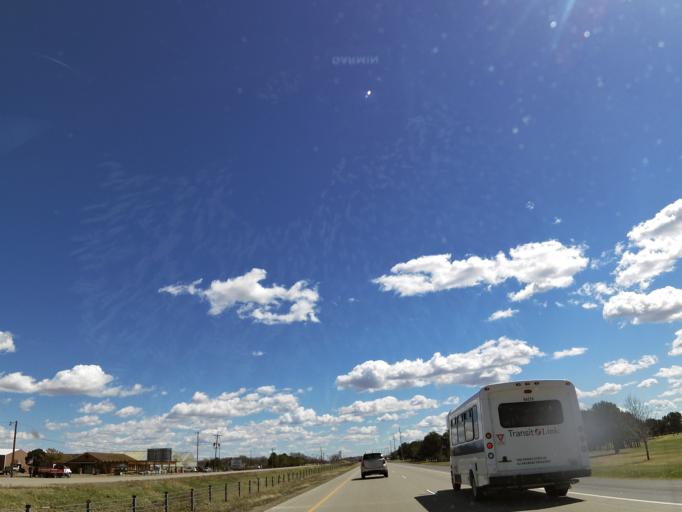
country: US
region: Minnesota
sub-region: Dakota County
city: Hastings
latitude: 44.7930
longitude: -92.8880
